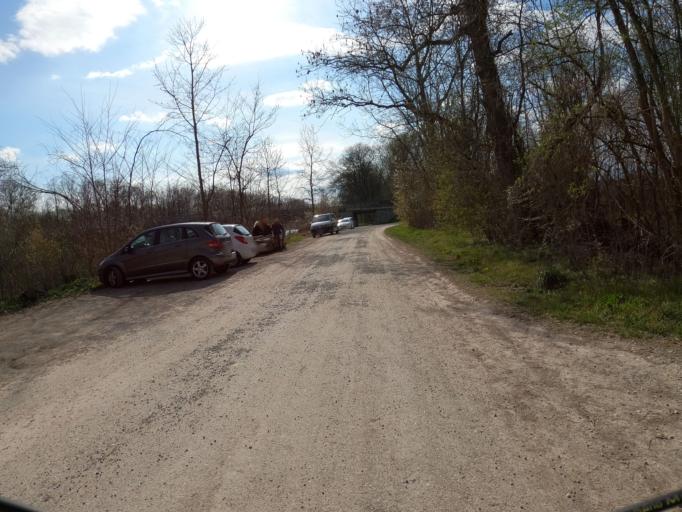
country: DE
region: Bavaria
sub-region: Swabia
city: Nersingen
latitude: 48.4345
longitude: 10.0627
